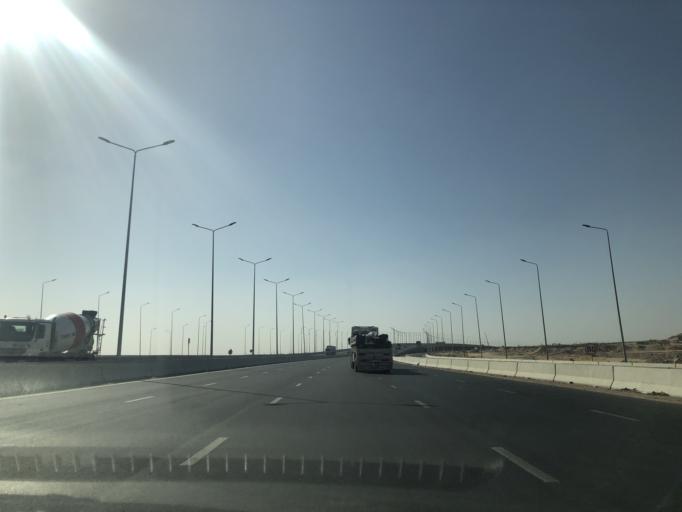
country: EG
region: Al Jizah
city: Madinat Sittah Uktubar
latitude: 29.9700
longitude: 30.8768
